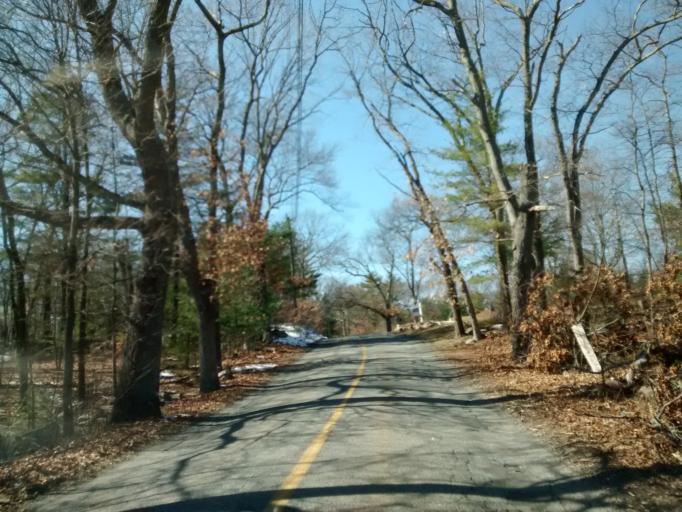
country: US
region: Massachusetts
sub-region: Worcester County
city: Northbridge
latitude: 42.1583
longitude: -71.6846
